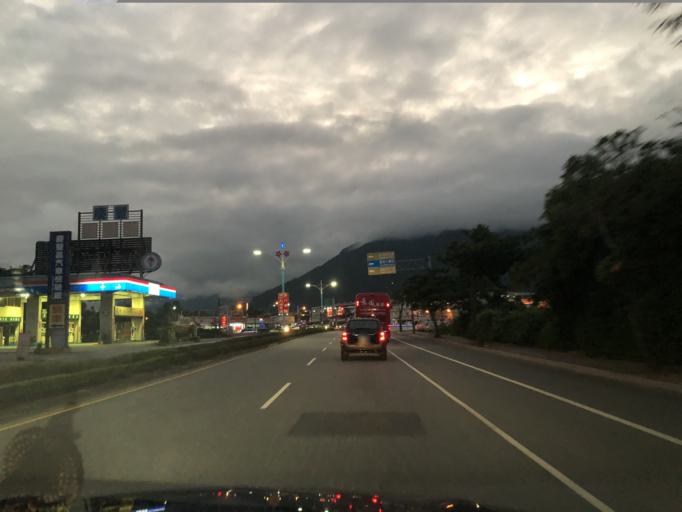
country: TW
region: Taiwan
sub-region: Hualien
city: Hualian
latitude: 23.9760
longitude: 121.5771
